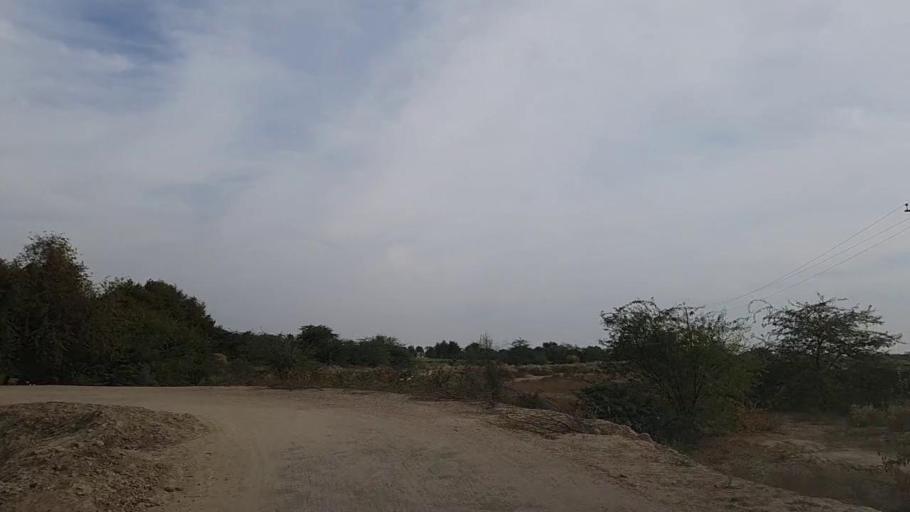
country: PK
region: Sindh
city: Jam Sahib
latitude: 26.4384
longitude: 68.6268
